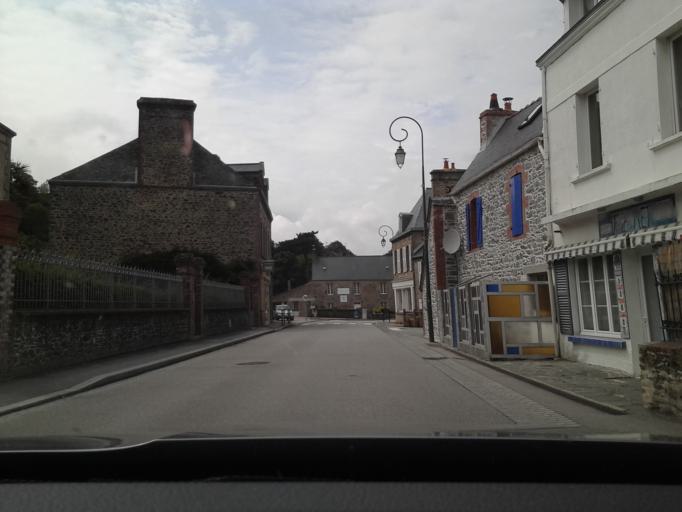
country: FR
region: Lower Normandy
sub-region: Departement de la Manche
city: Urville-Nacqueville
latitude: 49.6740
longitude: -1.7425
